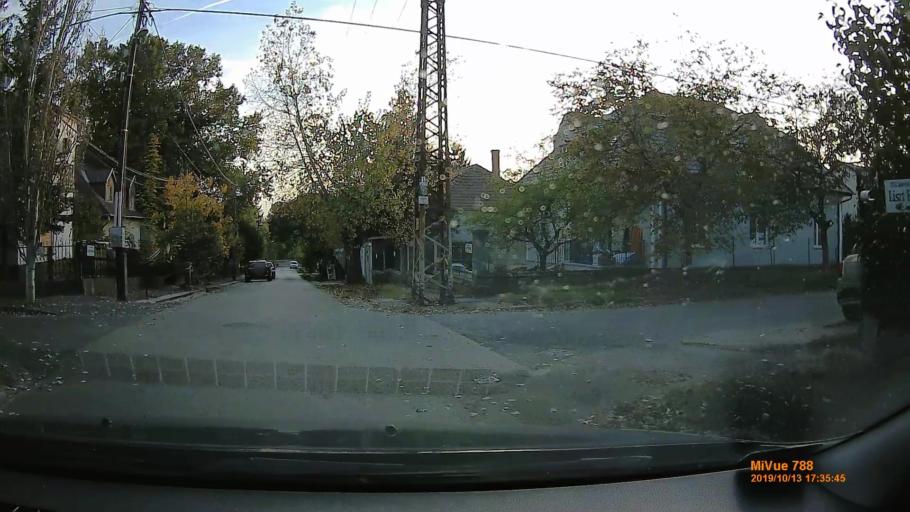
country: HU
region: Budapest
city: Budapest XVII. keruelet
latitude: 47.4885
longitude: 19.2520
